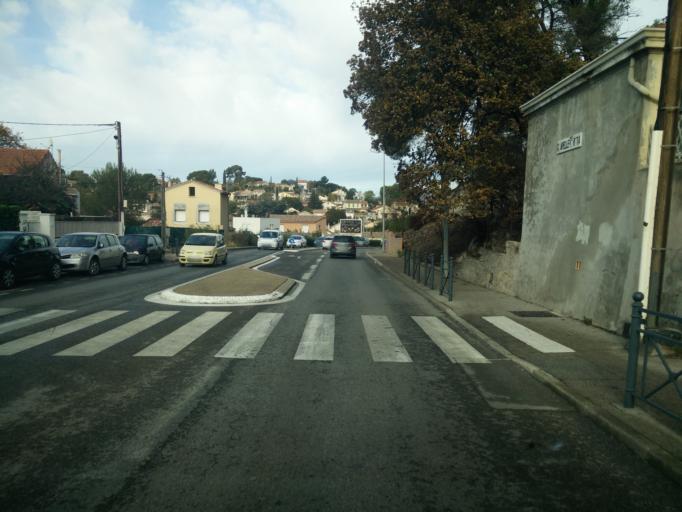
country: FR
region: Provence-Alpes-Cote d'Azur
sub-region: Departement du Var
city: La Seyne-sur-Mer
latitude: 43.0917
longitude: 5.8810
